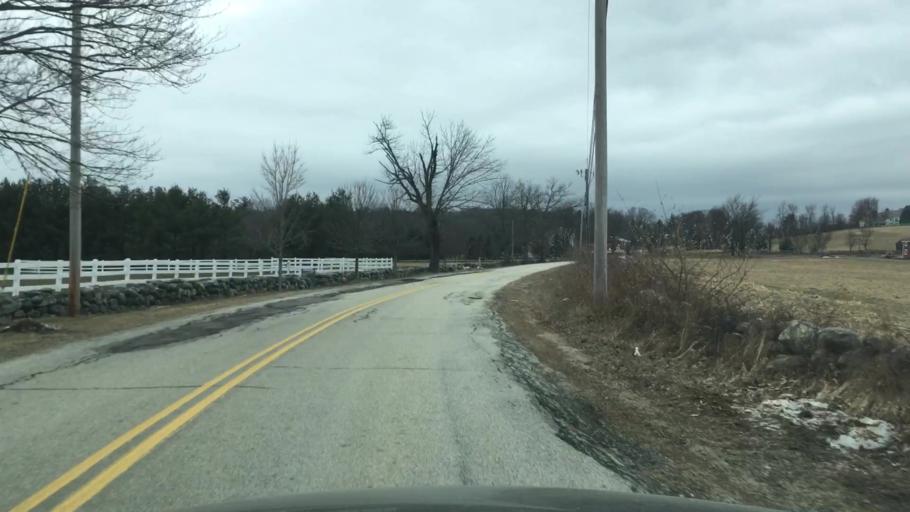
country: US
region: New Hampshire
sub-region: Hillsborough County
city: Mont Vernon
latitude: 42.9288
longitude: -71.6074
